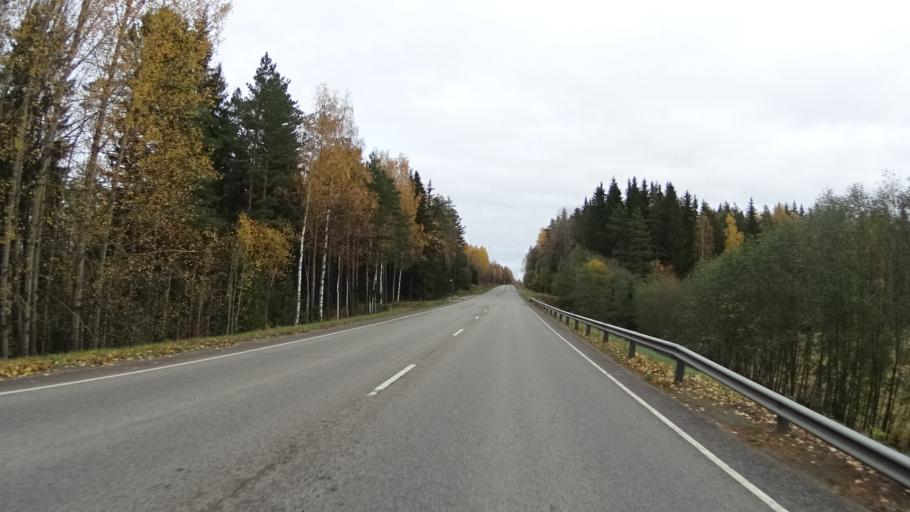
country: FI
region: South Karelia
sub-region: Lappeenranta
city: Lemi
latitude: 60.9708
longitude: 27.8505
